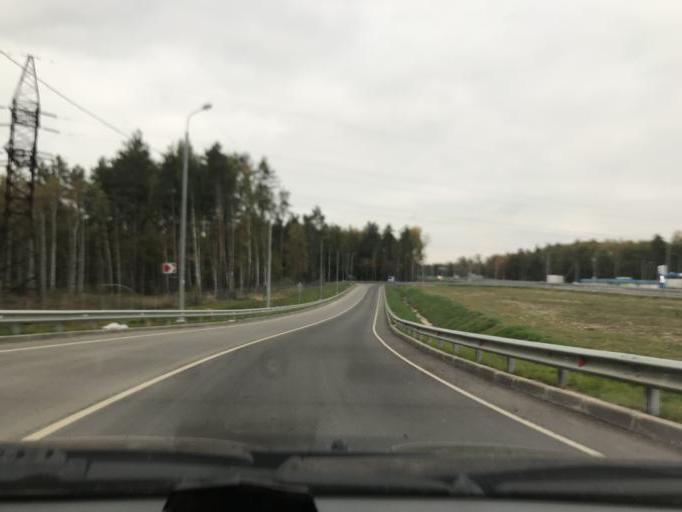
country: RU
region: Kaluga
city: Mstikhino
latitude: 54.6339
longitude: 36.1286
